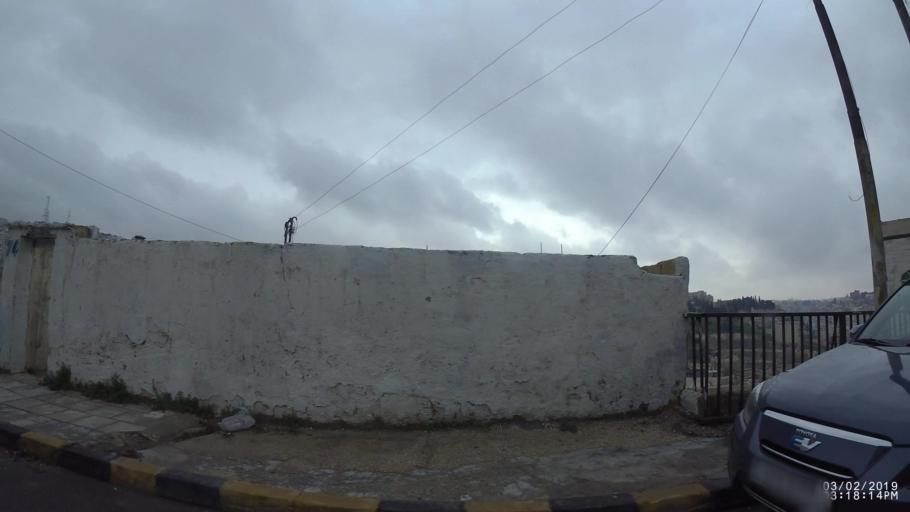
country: JO
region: Amman
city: Amman
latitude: 31.9508
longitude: 35.9407
